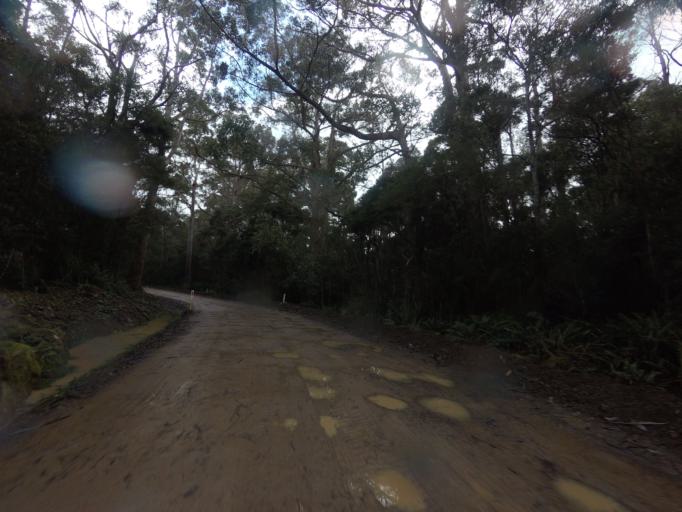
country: AU
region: Tasmania
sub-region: Huon Valley
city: Geeveston
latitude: -43.5763
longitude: 146.8882
